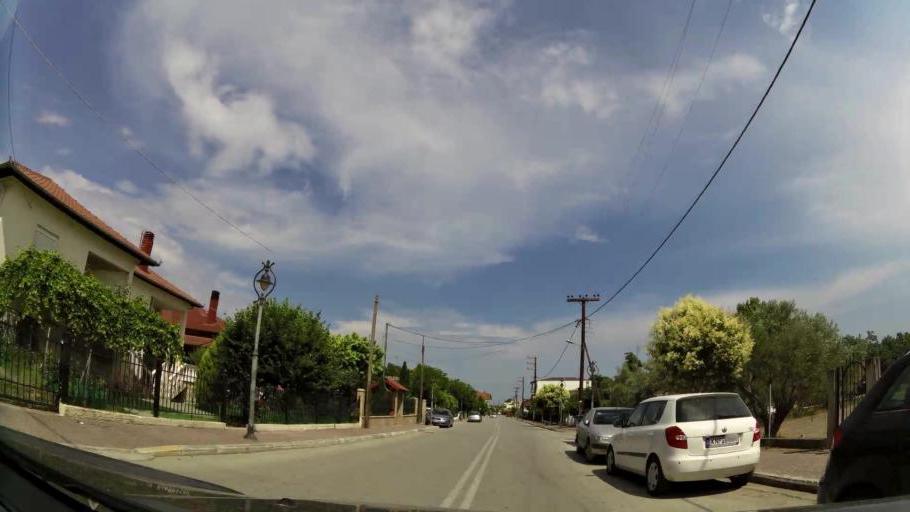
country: GR
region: Central Macedonia
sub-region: Nomos Pierias
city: Korinos
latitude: 40.3145
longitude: 22.5899
